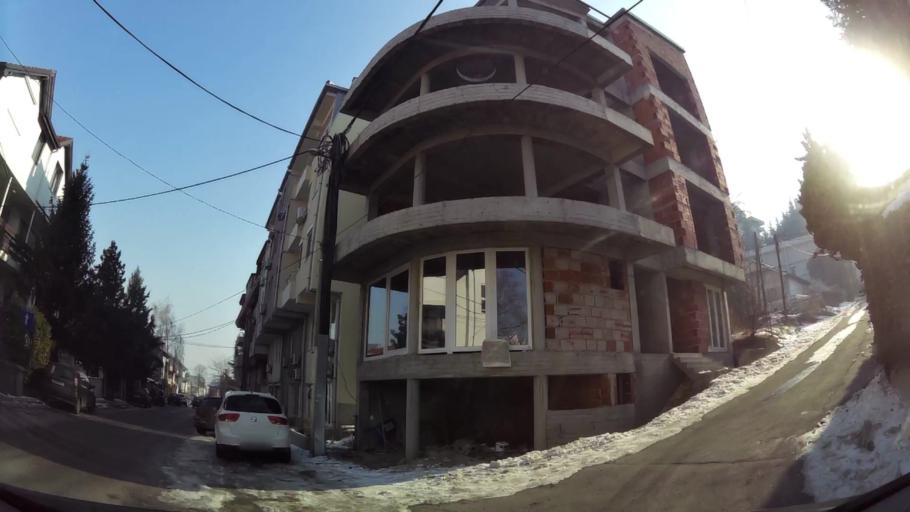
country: MK
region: Karpos
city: Skopje
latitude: 41.9861
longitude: 21.4213
